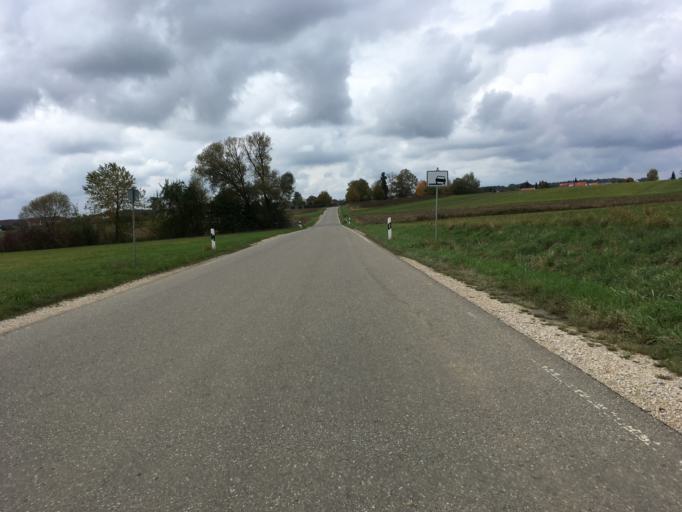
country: DE
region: Baden-Wuerttemberg
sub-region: Tuebingen Region
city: Gomaringen
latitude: 48.4784
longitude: 9.1108
